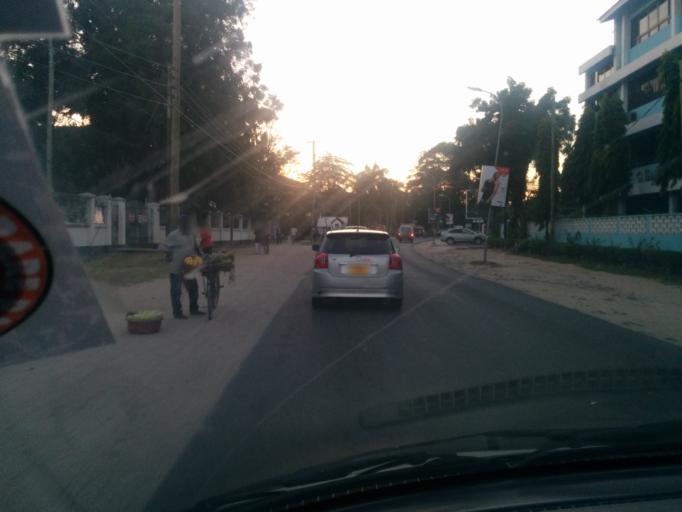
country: TZ
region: Dar es Salaam
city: Dar es Salaam
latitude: -6.8028
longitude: 39.2873
